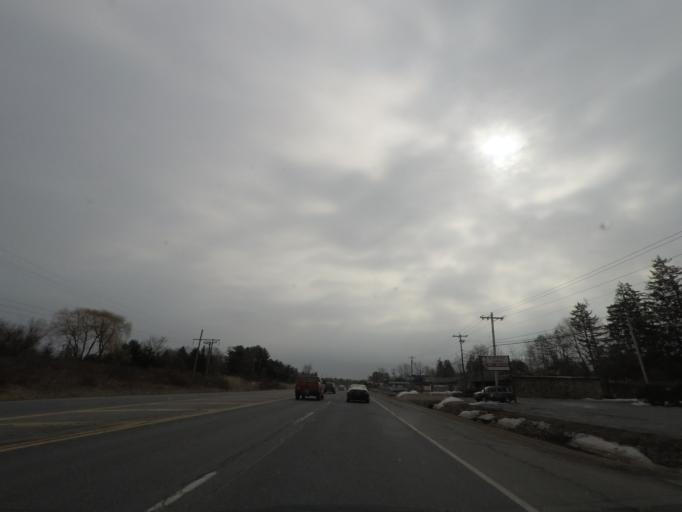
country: US
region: New York
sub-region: Warren County
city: Glens Falls
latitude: 43.3314
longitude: -73.6414
